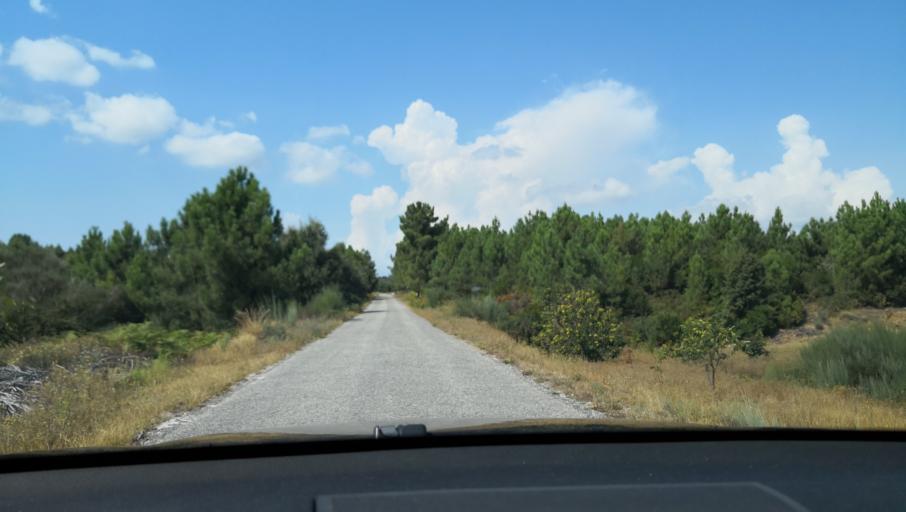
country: PT
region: Vila Real
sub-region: Sabrosa
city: Sabrosa
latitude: 41.3048
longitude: -7.5810
